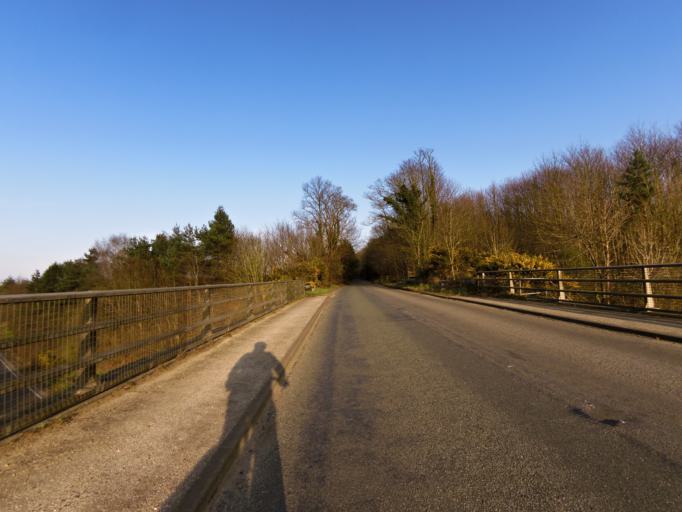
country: GB
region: England
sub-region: Suffolk
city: Kesgrave
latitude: 52.0792
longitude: 1.2706
